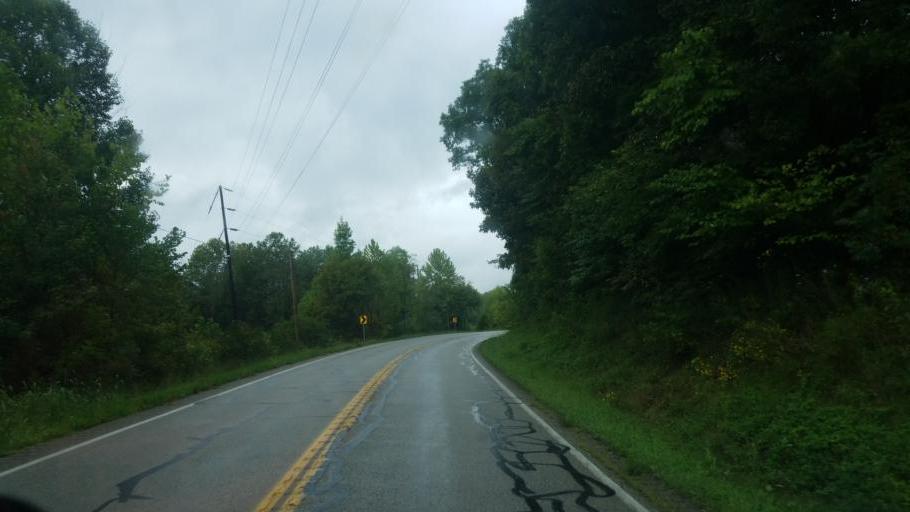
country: US
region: Kentucky
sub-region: Rowan County
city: Morehead
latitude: 38.1496
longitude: -83.4816
